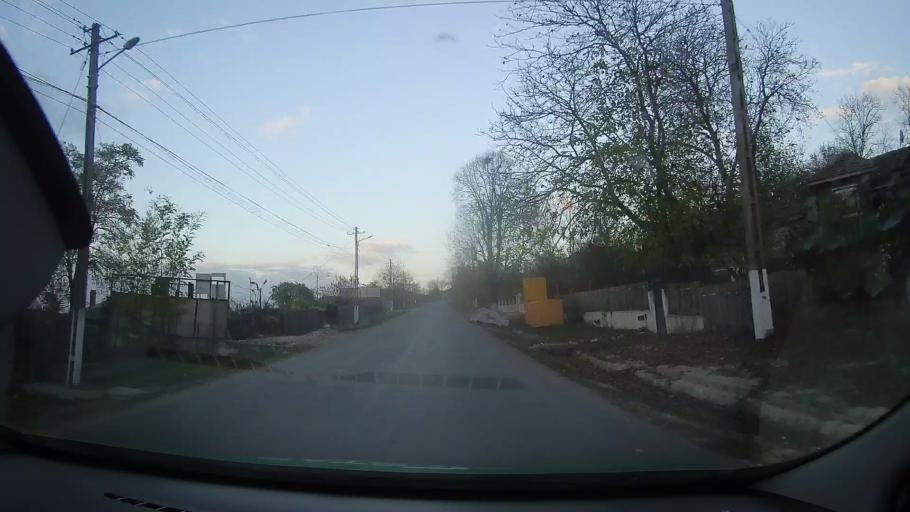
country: RO
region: Constanta
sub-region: Comuna Lipnita
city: Lipnita
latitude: 44.0952
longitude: 27.6079
